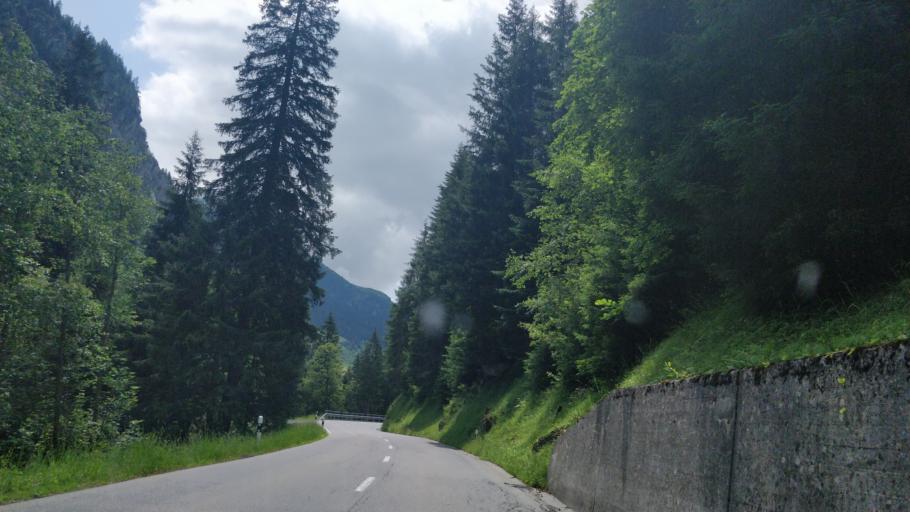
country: CH
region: Grisons
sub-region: Hinterrhein District
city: Hinterrhein
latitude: 46.6392
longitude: 9.1865
